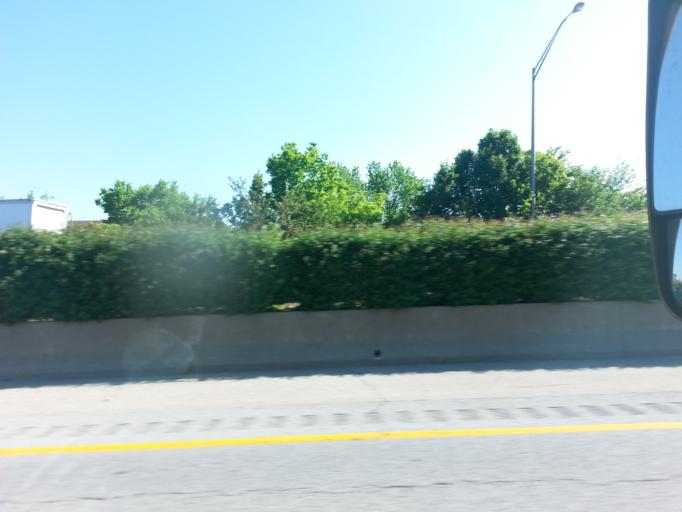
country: US
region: Kentucky
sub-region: Jefferson County
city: Hurstbourne Acres
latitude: 38.2239
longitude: -85.5808
